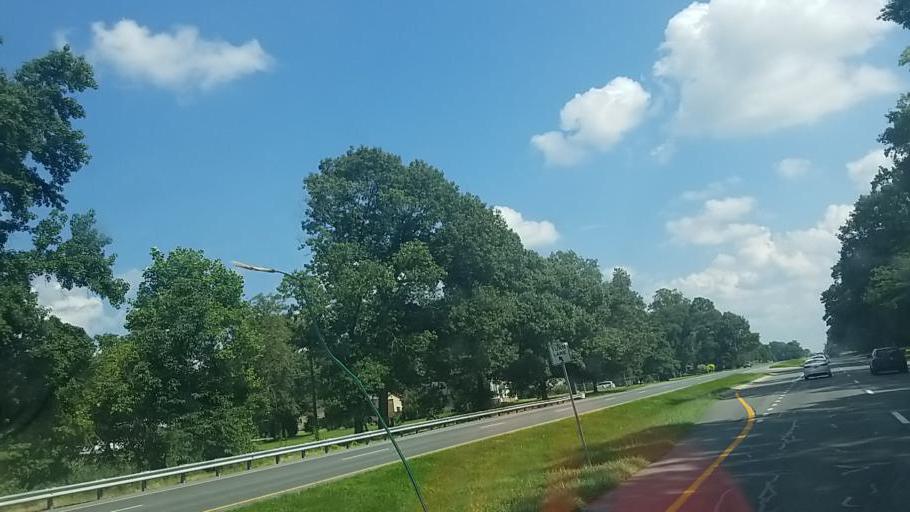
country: US
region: Delaware
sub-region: Sussex County
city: Georgetown
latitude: 38.6478
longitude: -75.3633
